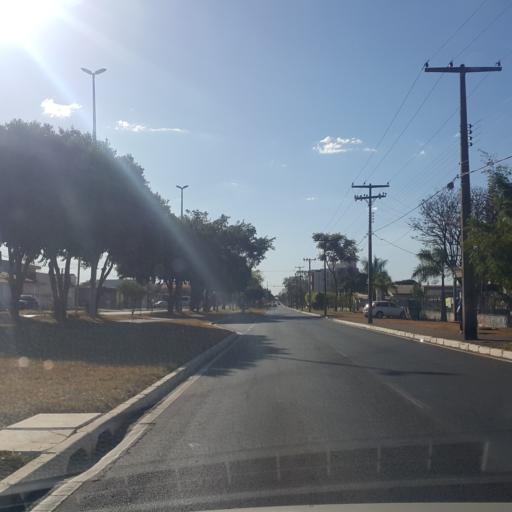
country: BR
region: Federal District
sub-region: Brasilia
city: Brasilia
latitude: -15.8060
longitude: -48.1036
